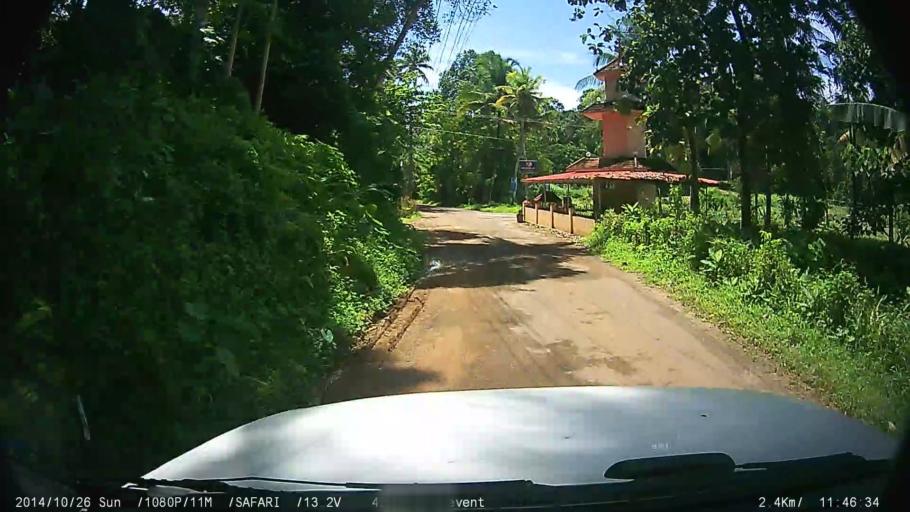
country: IN
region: Kerala
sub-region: Kottayam
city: Palackattumala
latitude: 9.7741
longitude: 76.5595
